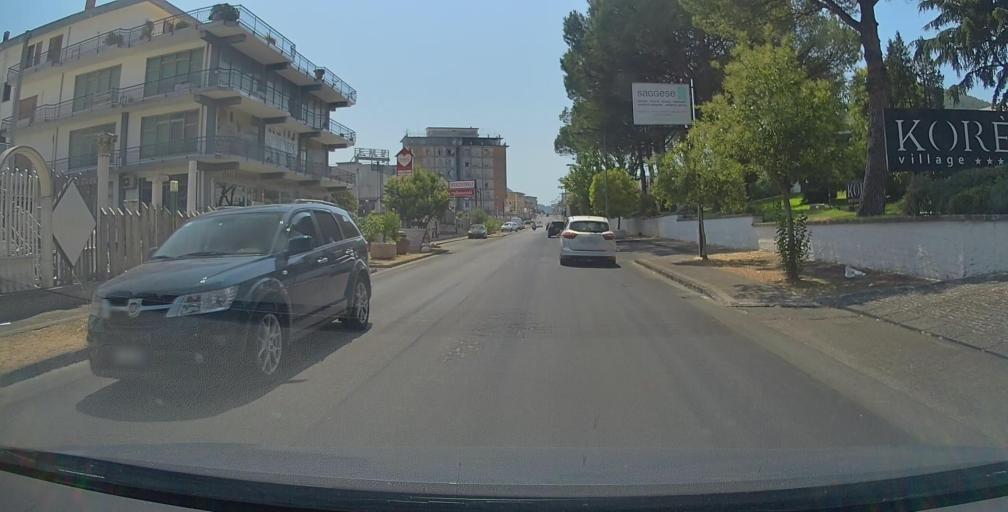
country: IT
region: Campania
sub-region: Provincia di Salerno
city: Nocera Superiore
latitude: 40.7311
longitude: 14.6877
